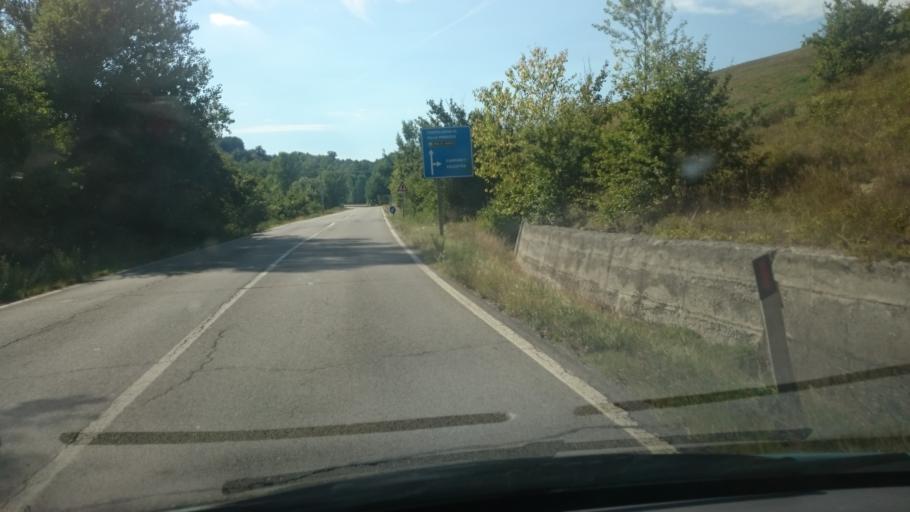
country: IT
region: Emilia-Romagna
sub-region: Provincia di Reggio Emilia
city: Toano
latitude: 44.4125
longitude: 10.5898
